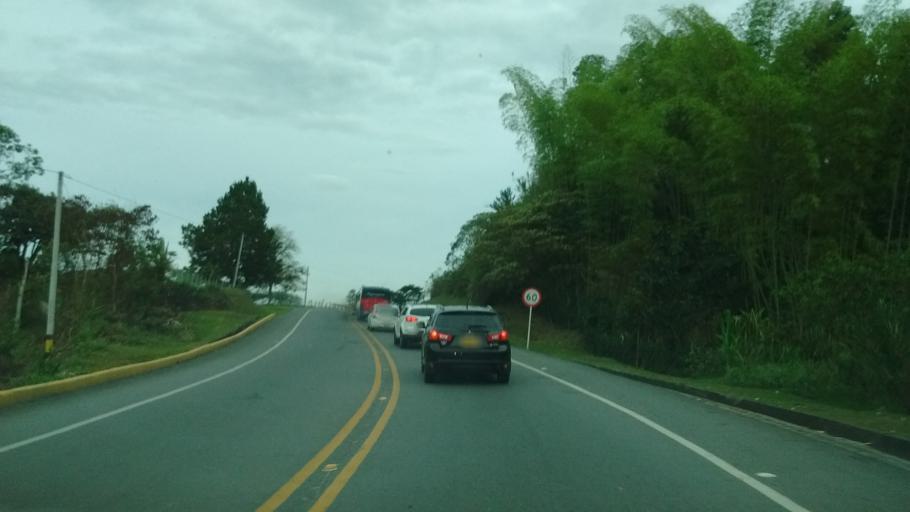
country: CO
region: Cauca
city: Morales
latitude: 2.7282
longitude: -76.5444
